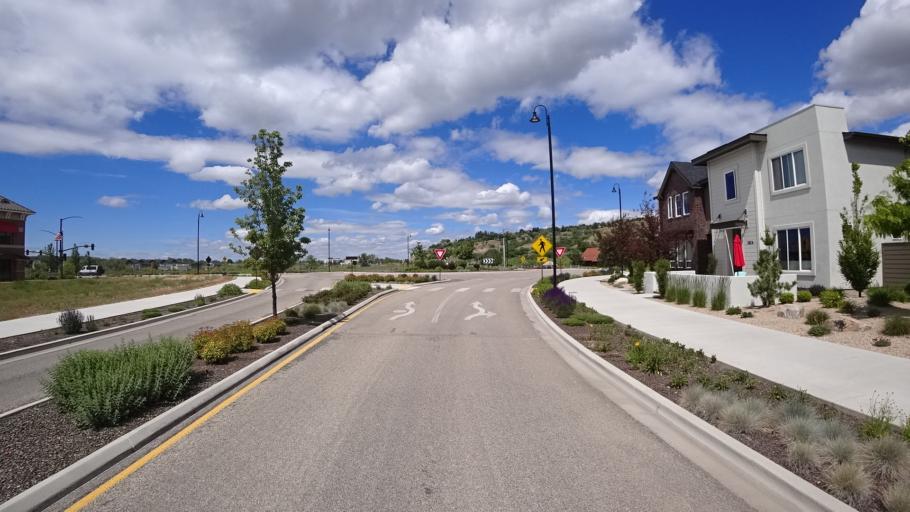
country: US
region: Idaho
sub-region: Ada County
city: Boise
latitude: 43.5763
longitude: -116.1391
